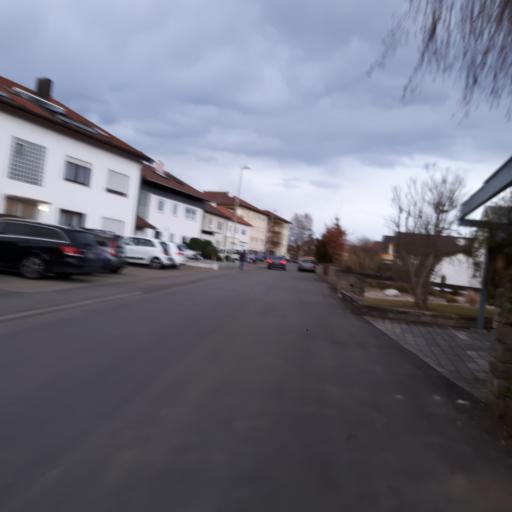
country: DE
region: Baden-Wuerttemberg
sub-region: Regierungsbezirk Stuttgart
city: Pleidelsheim
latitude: 48.9637
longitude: 9.2023
